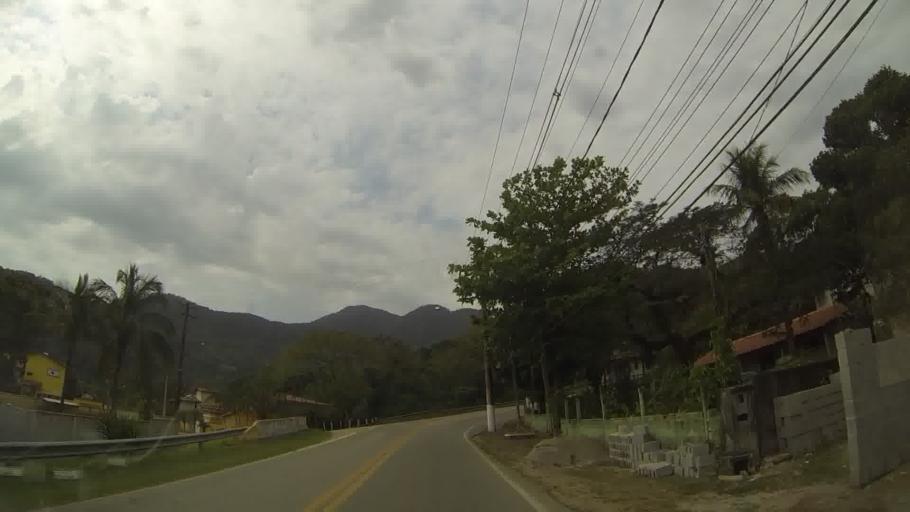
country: BR
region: Sao Paulo
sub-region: Sao Sebastiao
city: Sao Sebastiao
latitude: -23.7930
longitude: -45.5527
